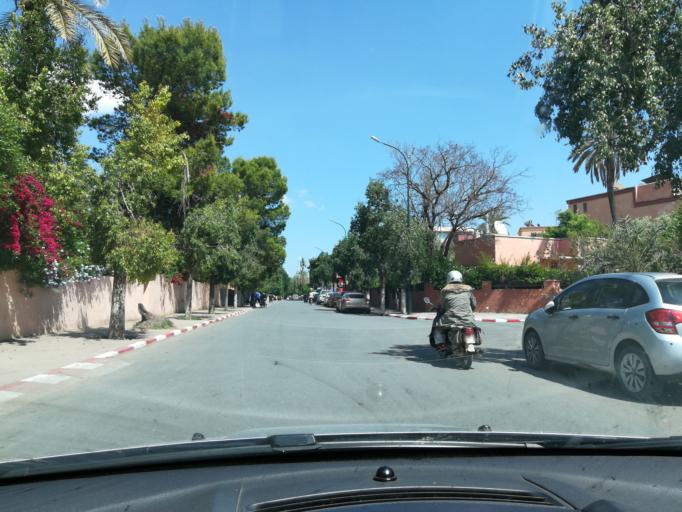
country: MA
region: Marrakech-Tensift-Al Haouz
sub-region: Marrakech
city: Marrakesh
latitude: 31.6408
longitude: -8.0166
